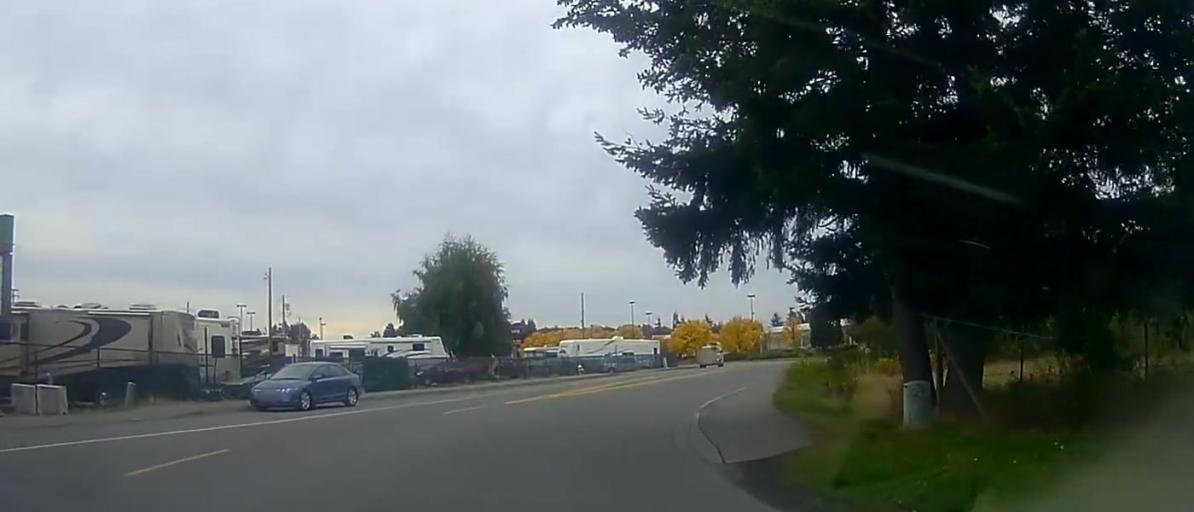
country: US
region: Washington
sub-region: Skagit County
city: Mount Vernon
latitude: 48.4405
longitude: -122.3376
